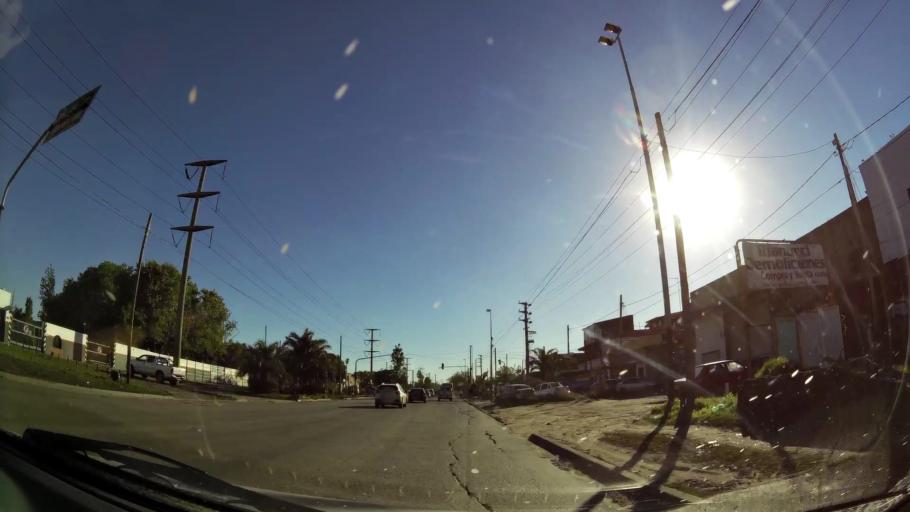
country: AR
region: Buenos Aires
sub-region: Partido de Quilmes
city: Quilmes
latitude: -34.7443
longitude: -58.3274
